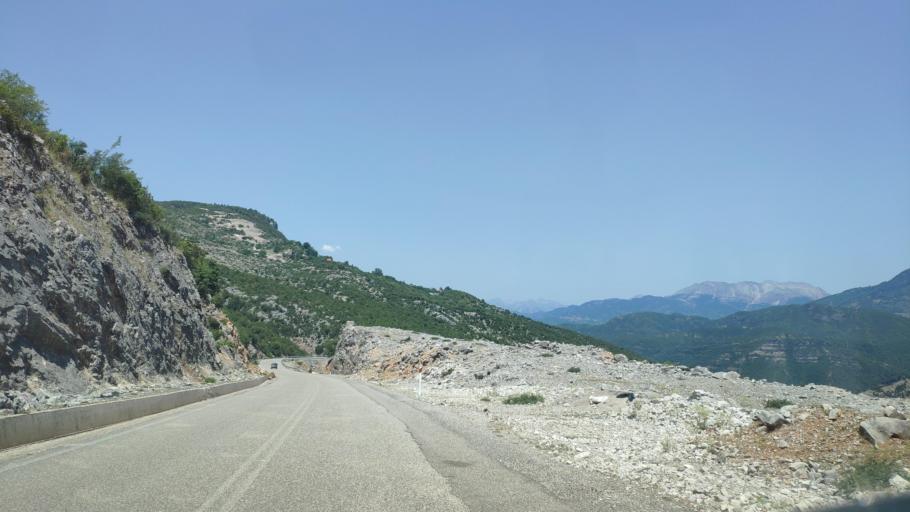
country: GR
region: Thessaly
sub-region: Nomos Kardhitsas
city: Anthiro
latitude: 39.1388
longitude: 21.3896
